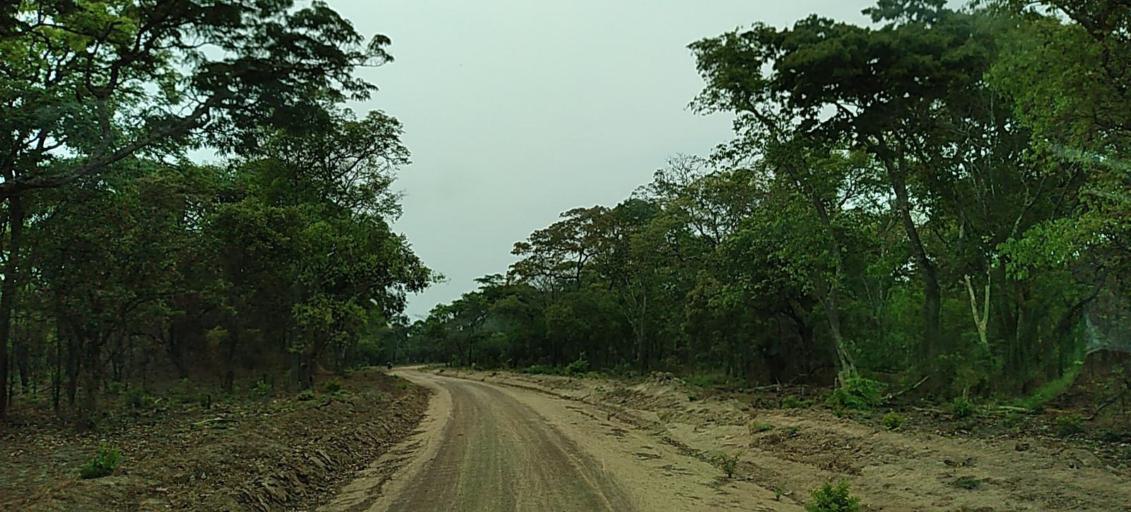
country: ZM
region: North-Western
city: Solwezi
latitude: -12.5210
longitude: 26.5239
